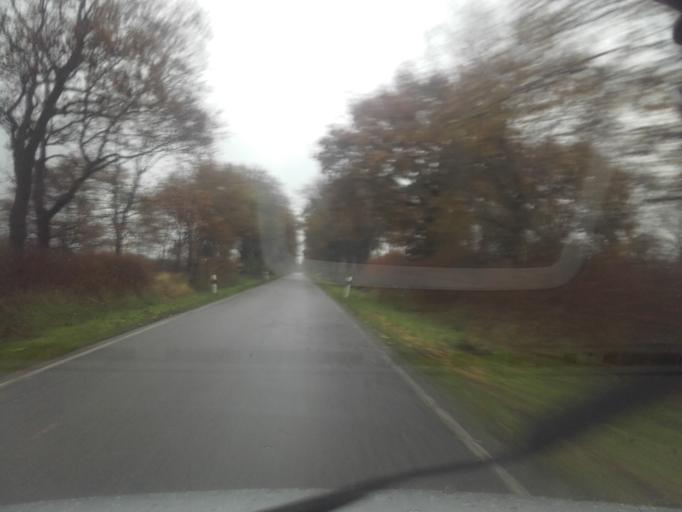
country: DE
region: Schleswig-Holstein
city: Alt Bennebek
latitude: 54.3971
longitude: 9.4128
